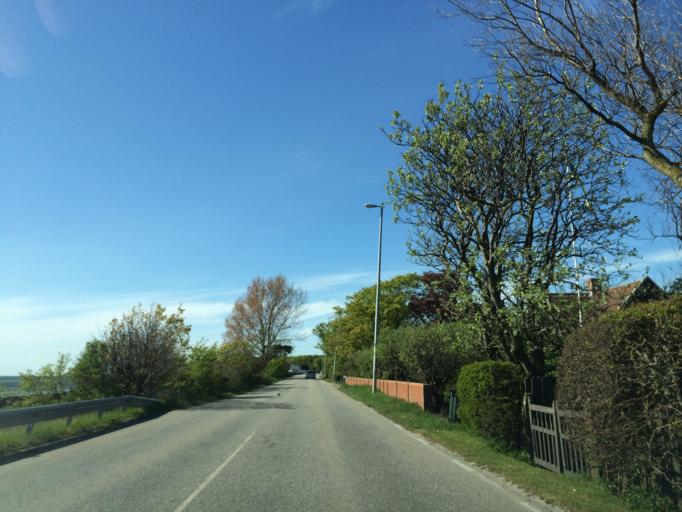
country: SE
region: Skane
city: Bjarred
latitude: 55.7028
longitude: 13.0431
